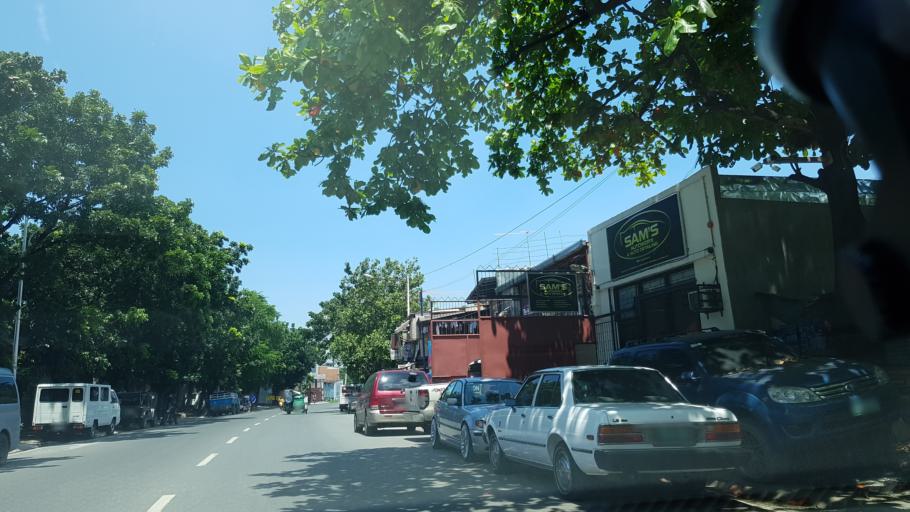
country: PH
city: Sambayanihan People's Village
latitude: 14.4681
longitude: 120.9965
